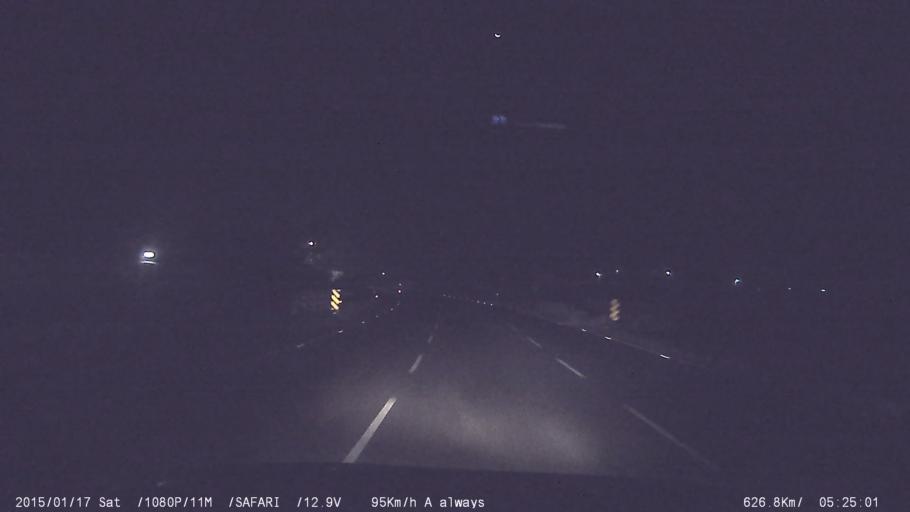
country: IN
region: Tamil Nadu
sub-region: Vellore
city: Katpadi
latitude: 12.9447
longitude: 79.2279
